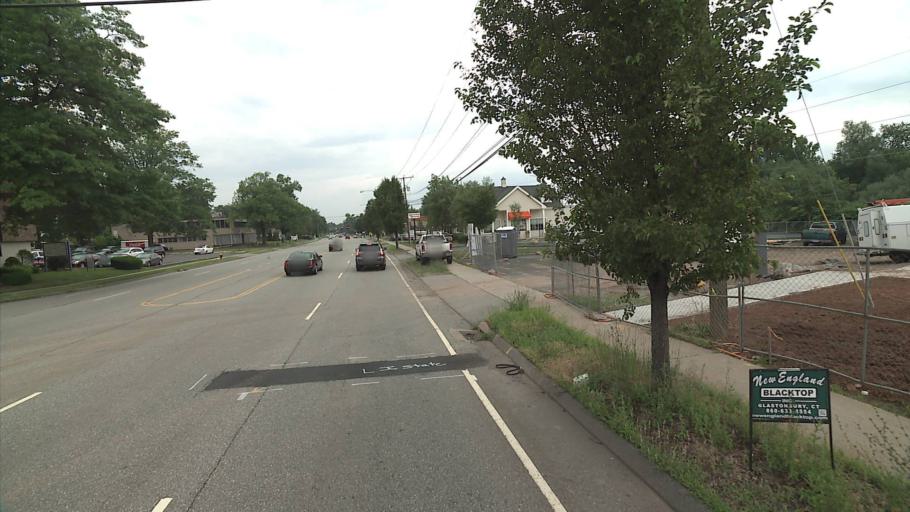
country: US
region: Connecticut
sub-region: Hartford County
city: Wethersfield
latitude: 41.7144
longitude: -72.6642
